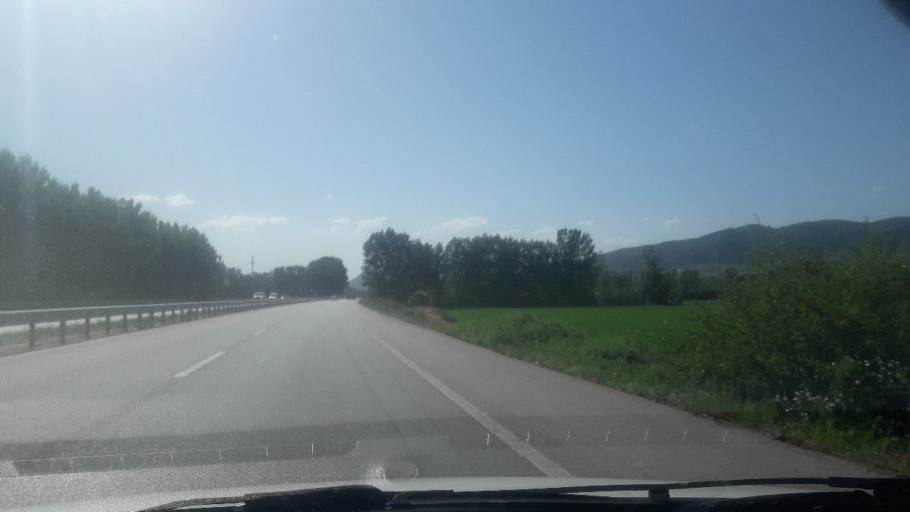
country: TR
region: Tokat
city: Dokmetepe
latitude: 40.3051
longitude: 36.3085
